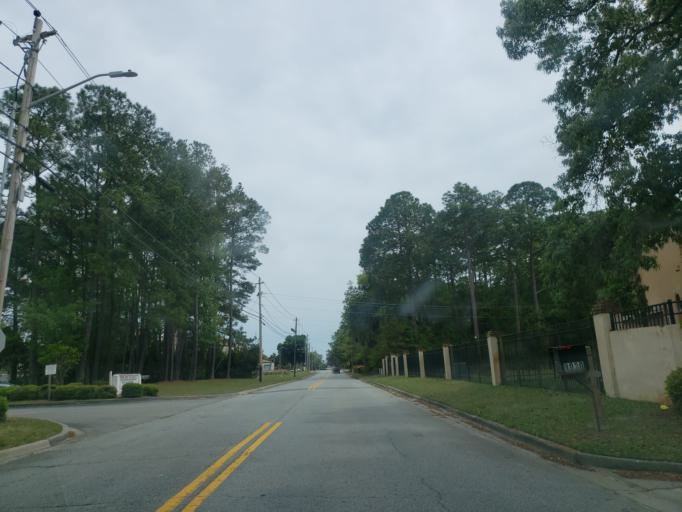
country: US
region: Georgia
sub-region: Chatham County
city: Montgomery
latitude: 31.9899
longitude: -81.1618
